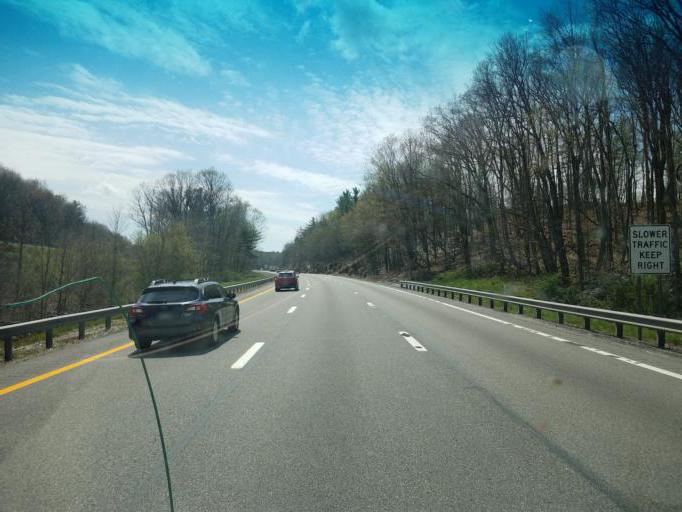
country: US
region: West Virginia
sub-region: Raleigh County
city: Shady Spring
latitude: 37.6632
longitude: -81.1159
